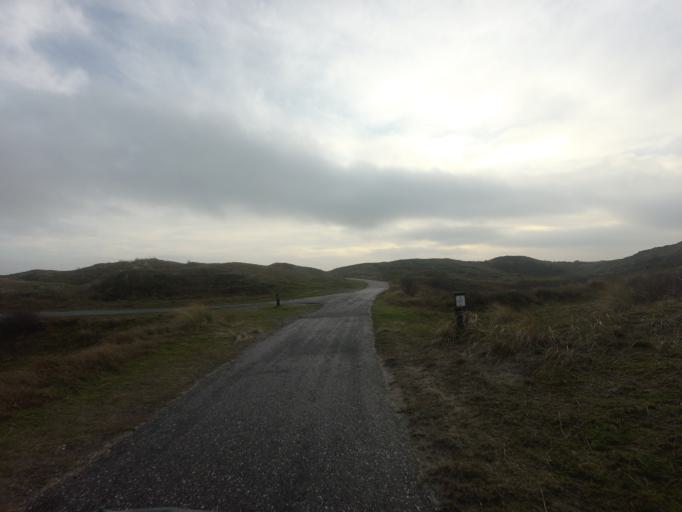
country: NL
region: North Holland
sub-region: Gemeente Texel
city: Den Burg
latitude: 53.1554
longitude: 4.8414
